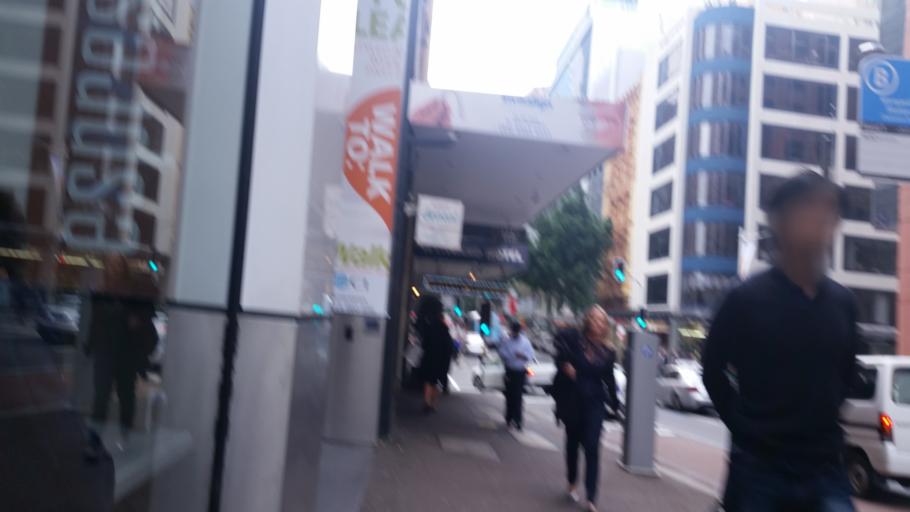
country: AU
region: New South Wales
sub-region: City of Sydney
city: Sydney
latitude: -33.8669
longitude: 151.2052
